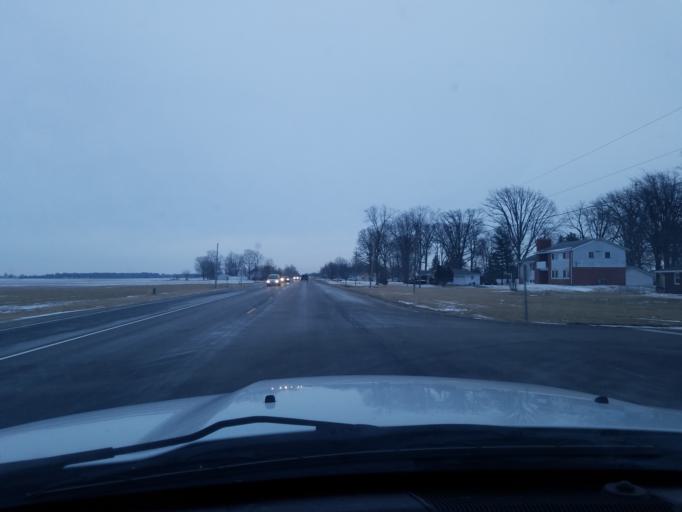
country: US
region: Indiana
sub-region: Randolph County
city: Parker City
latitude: 40.1932
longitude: -85.1852
